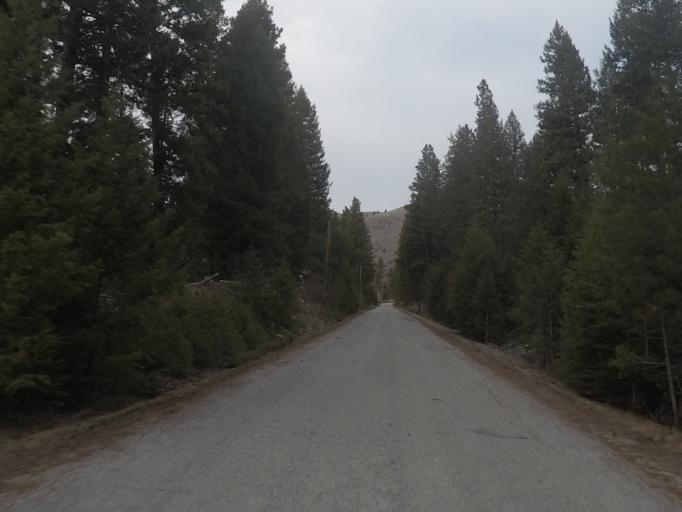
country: US
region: Montana
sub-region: Ravalli County
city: Hamilton
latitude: 45.8504
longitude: -114.0326
